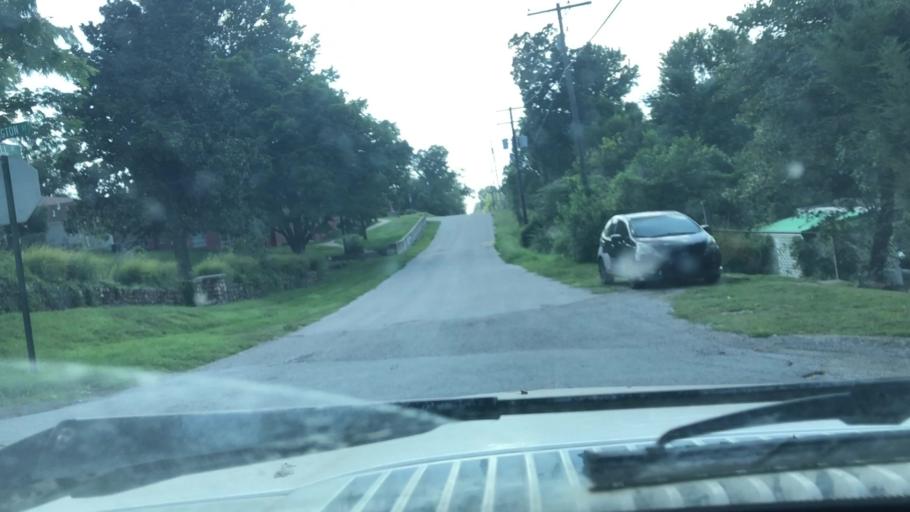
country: US
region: Missouri
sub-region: Newton County
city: Neosho
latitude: 36.8644
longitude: -94.3676
